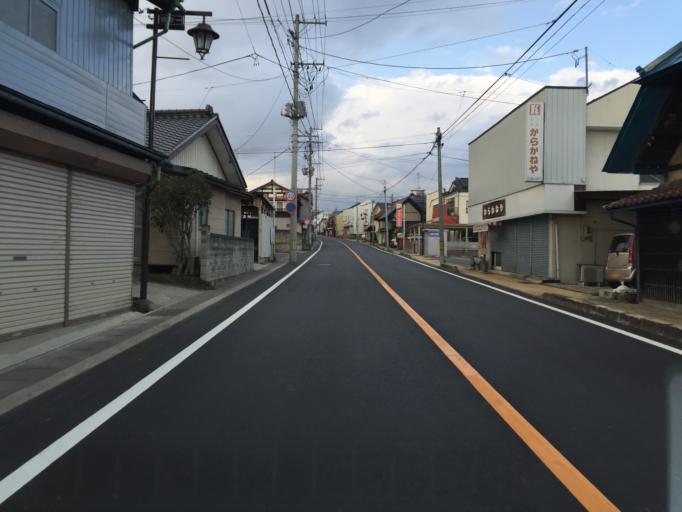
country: JP
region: Fukushima
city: Koriyama
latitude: 37.4445
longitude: 140.3905
